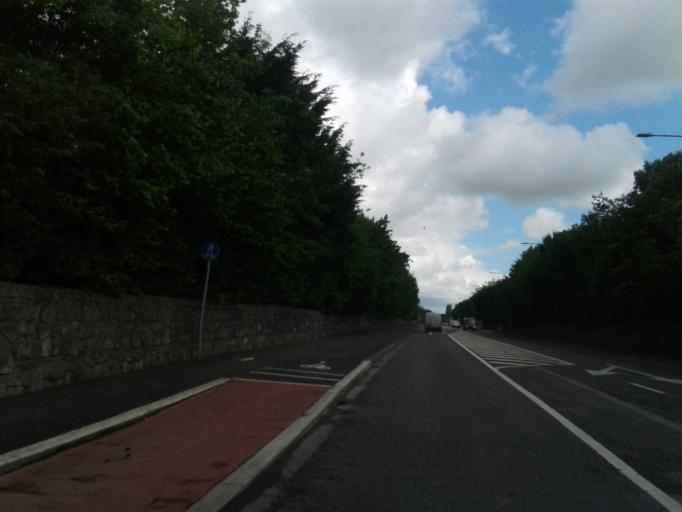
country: IE
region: Leinster
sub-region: Kildare
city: Maynooth
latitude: 53.3708
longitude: -6.5904
